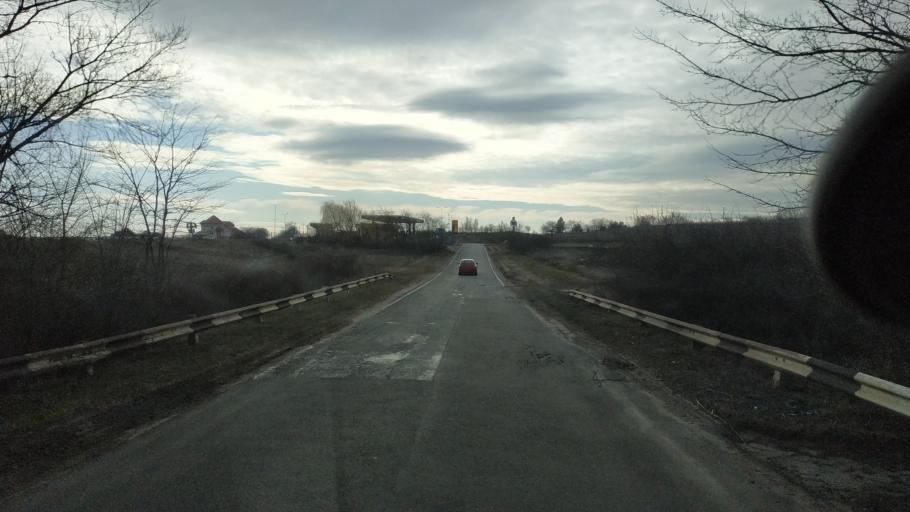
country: MD
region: Chisinau
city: Vadul lui Voda
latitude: 47.0726
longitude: 29.0196
